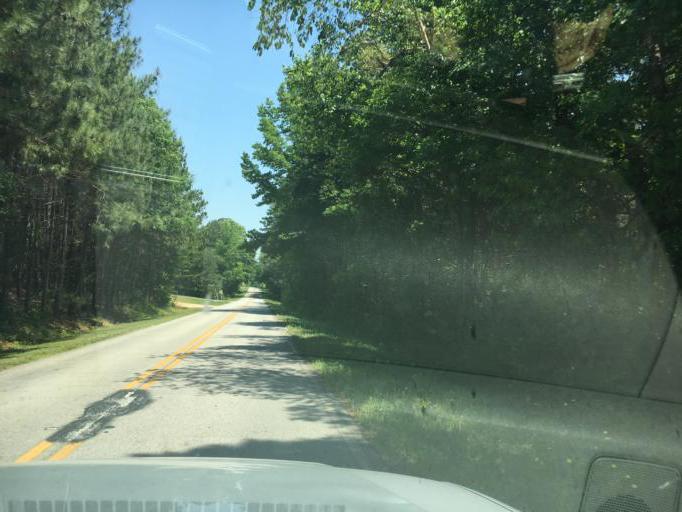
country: US
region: Georgia
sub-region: Hart County
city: Royston
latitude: 34.3084
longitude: -83.0977
